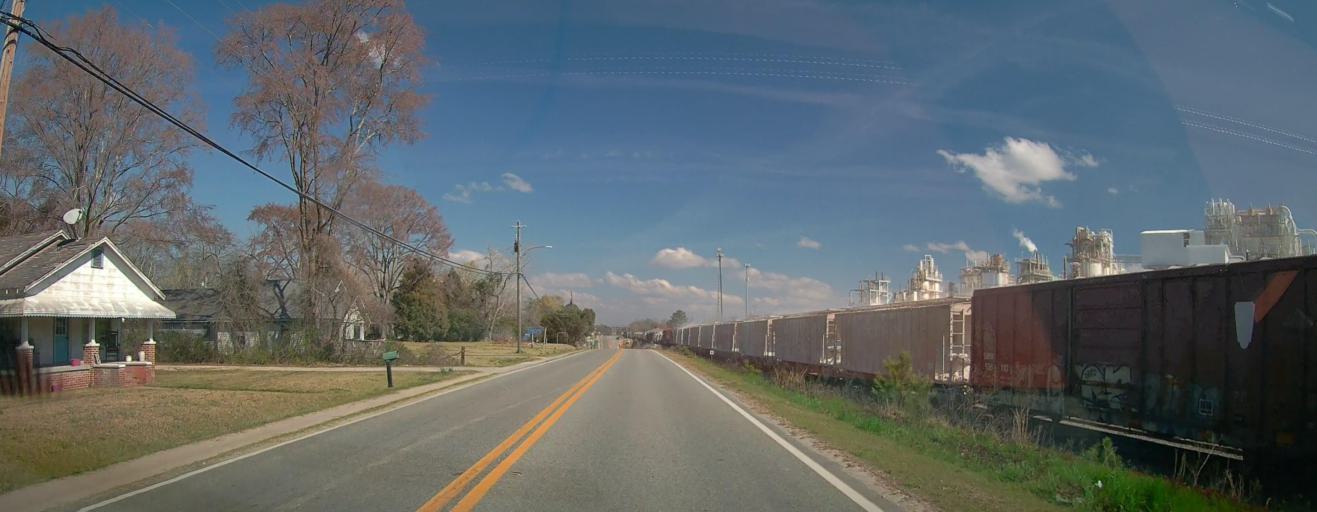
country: US
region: Georgia
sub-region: Wilkinson County
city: Gordon
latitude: 32.8826
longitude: -83.3407
